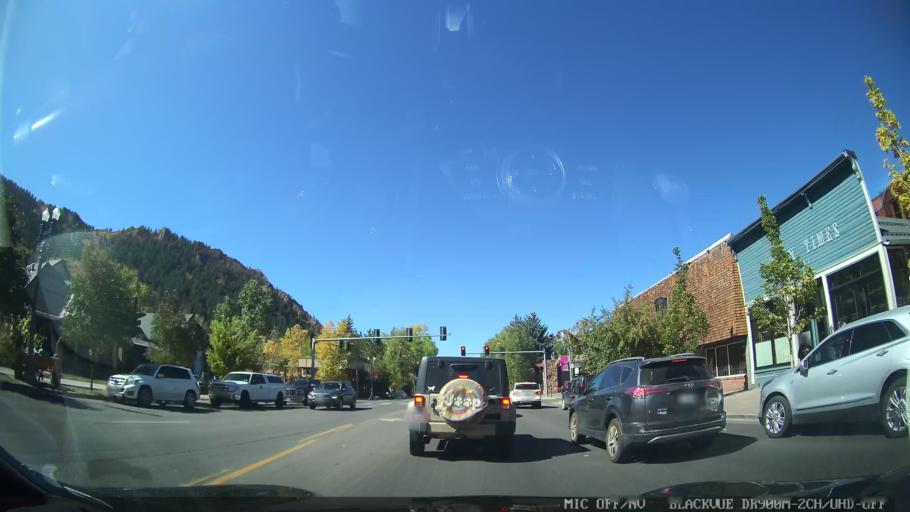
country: US
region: Colorado
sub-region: Pitkin County
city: Aspen
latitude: 39.1908
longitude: -106.8199
